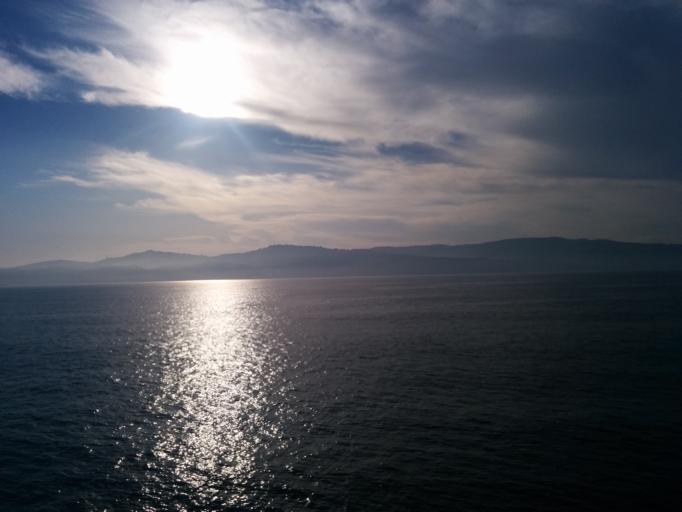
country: MA
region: Tanger-Tetouan
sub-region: Tanger-Assilah
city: Tangier
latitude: 35.8076
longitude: -5.7830
